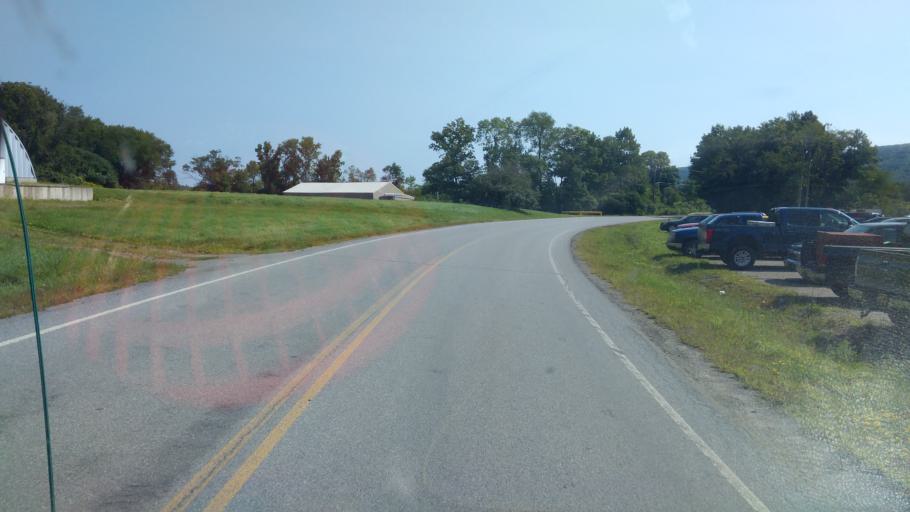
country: US
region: New York
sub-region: Allegany County
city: Friendship
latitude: 42.2148
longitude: -78.1163
